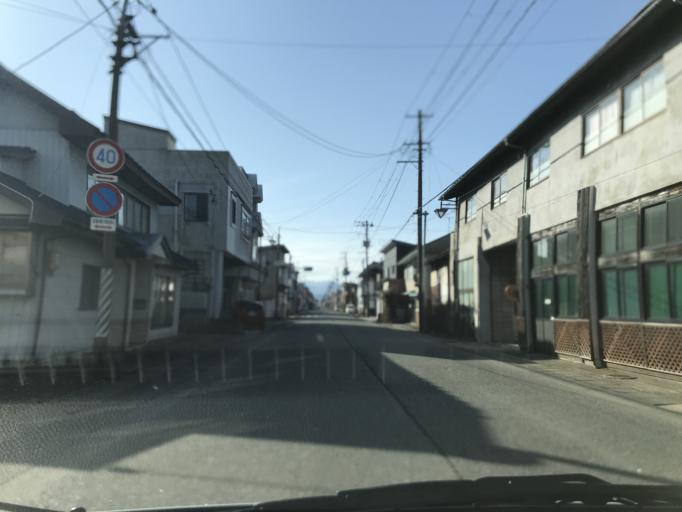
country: JP
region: Iwate
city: Kitakami
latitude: 39.3001
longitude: 141.0405
